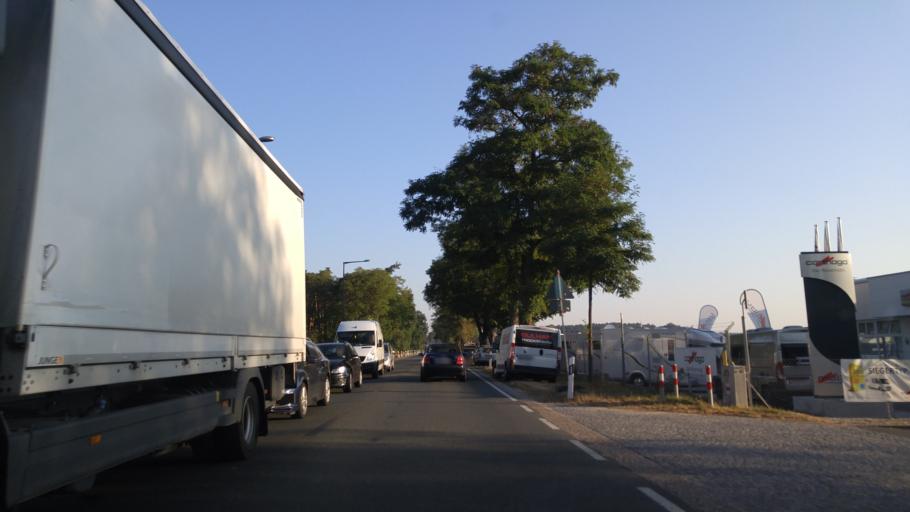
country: DE
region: Bavaria
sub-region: Regierungsbezirk Mittelfranken
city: Furth
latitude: 49.5181
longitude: 10.9758
